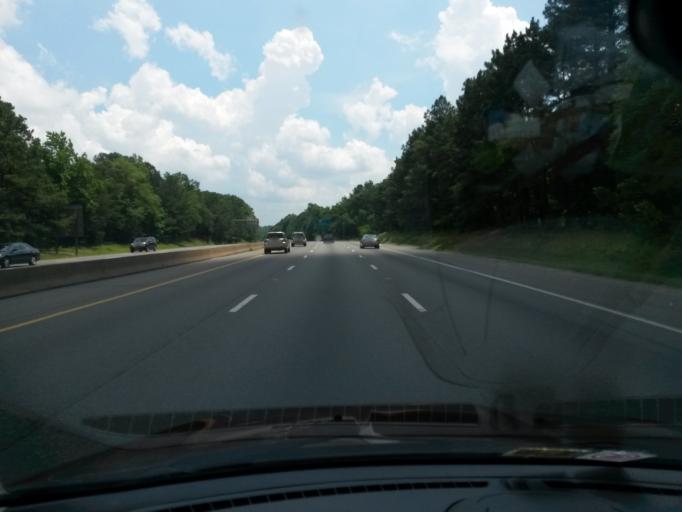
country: US
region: Virginia
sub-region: Chesterfield County
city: Chester
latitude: 37.3870
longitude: -77.4196
